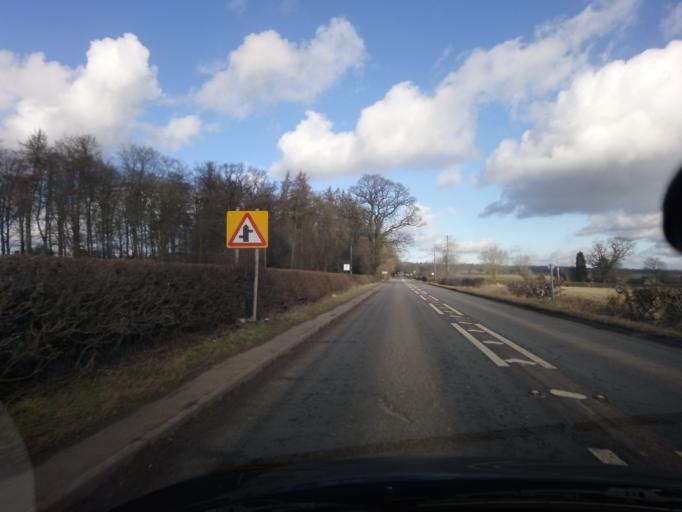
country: GB
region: England
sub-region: Shropshire
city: Clive
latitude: 52.7845
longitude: -2.7061
